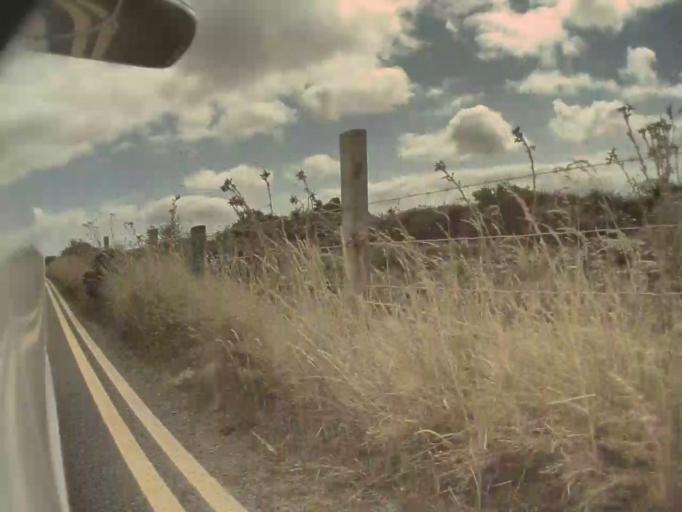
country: IE
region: Leinster
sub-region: Wicklow
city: Kilmacanoge
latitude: 53.1459
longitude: -6.1622
